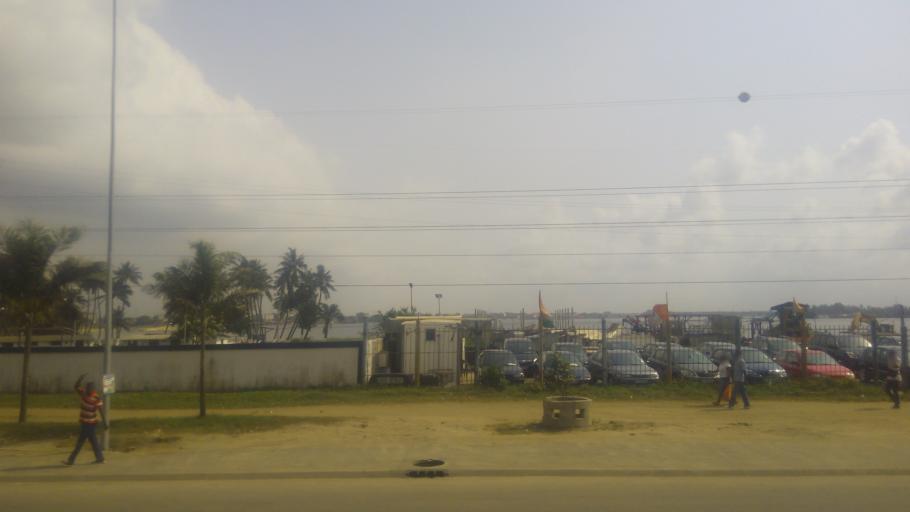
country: CI
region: Lagunes
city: Abidjan
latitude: 5.2749
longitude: -3.9655
